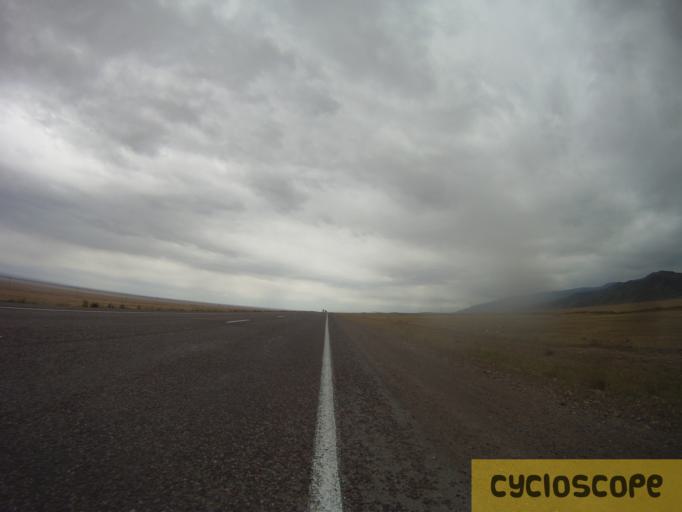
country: KG
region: Chuy
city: Ivanovka
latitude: 43.3834
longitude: 75.1829
